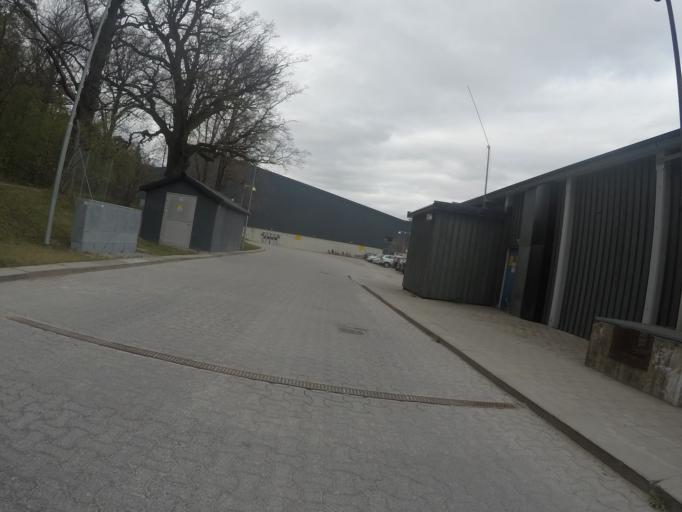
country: SE
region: Vaestmanland
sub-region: Vasteras
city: Vasteras
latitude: 59.6252
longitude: 16.5294
